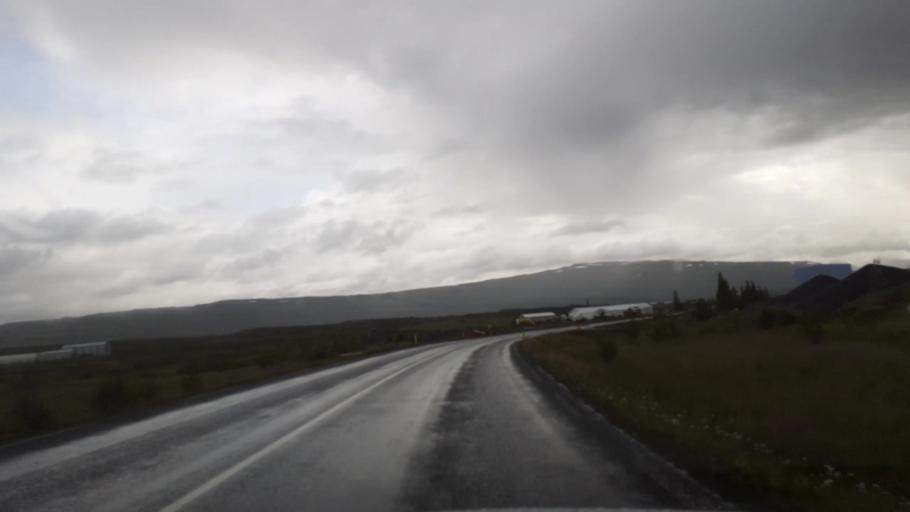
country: IS
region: East
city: Egilsstadir
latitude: 65.2991
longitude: -14.4495
